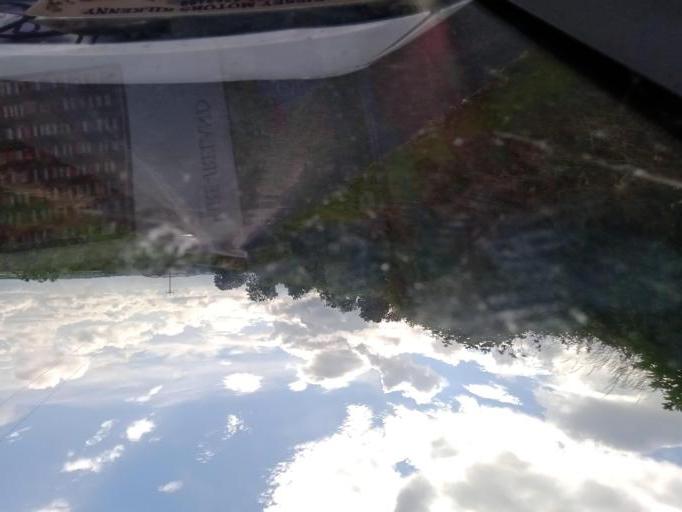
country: IE
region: Leinster
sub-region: Laois
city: Rathdowney
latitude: 52.7730
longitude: -7.5104
